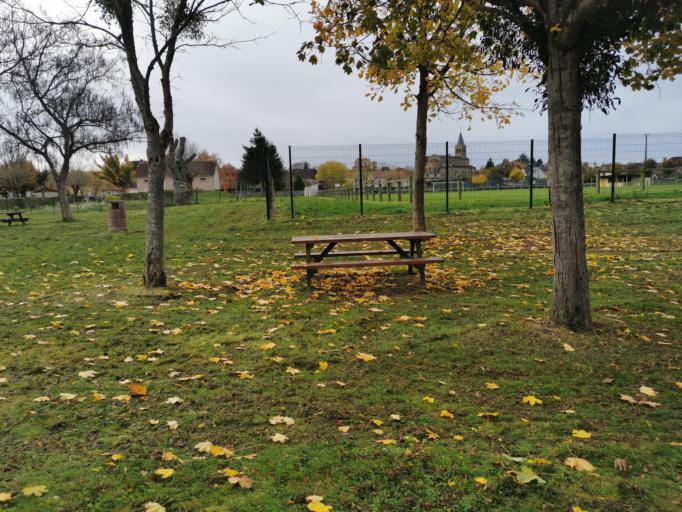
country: FR
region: Auvergne
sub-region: Departement de l'Allier
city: Diou
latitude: 46.5365
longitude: 3.7433
